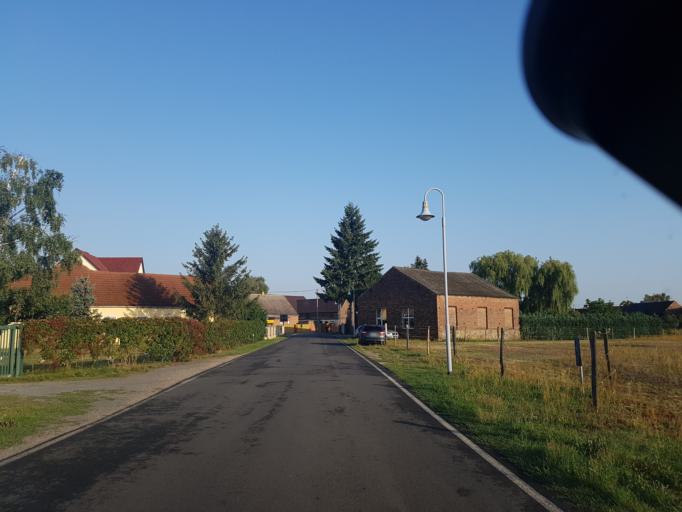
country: DE
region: Saxony-Anhalt
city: Holzdorf
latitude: 51.8285
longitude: 13.1240
